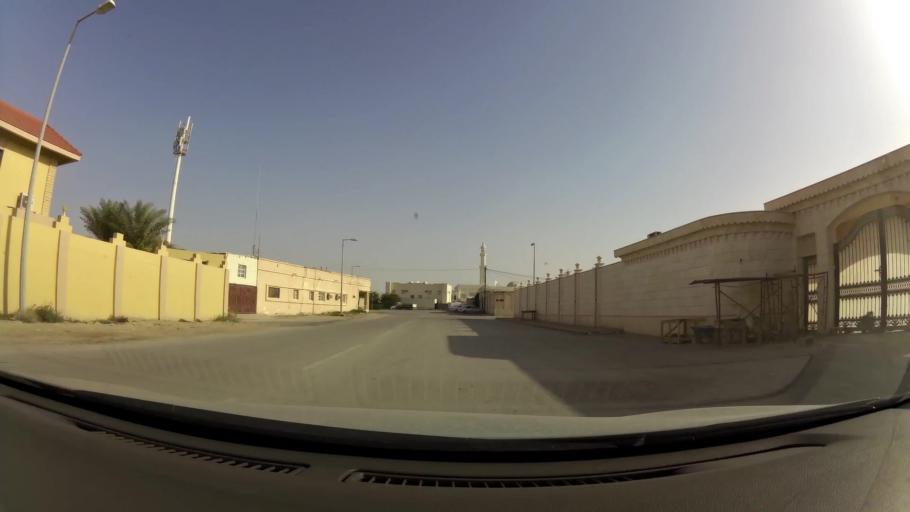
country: QA
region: Baladiyat ar Rayyan
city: Ar Rayyan
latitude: 25.3333
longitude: 51.4428
